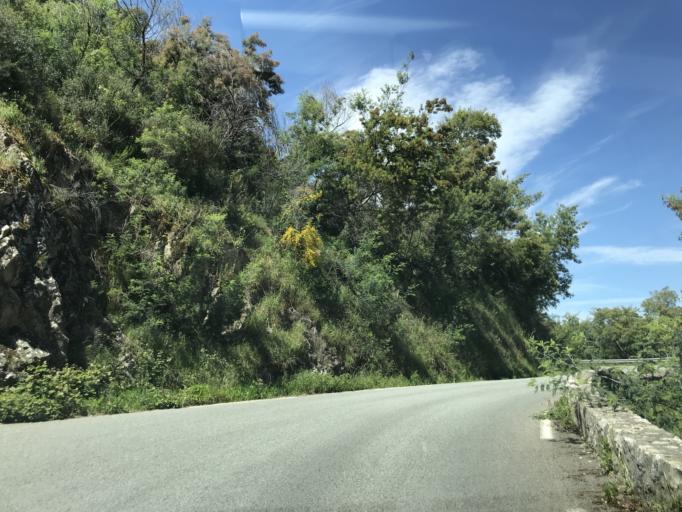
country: FR
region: Provence-Alpes-Cote d'Azur
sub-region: Departement du Var
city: Tanneron
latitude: 43.5853
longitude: 6.8958
